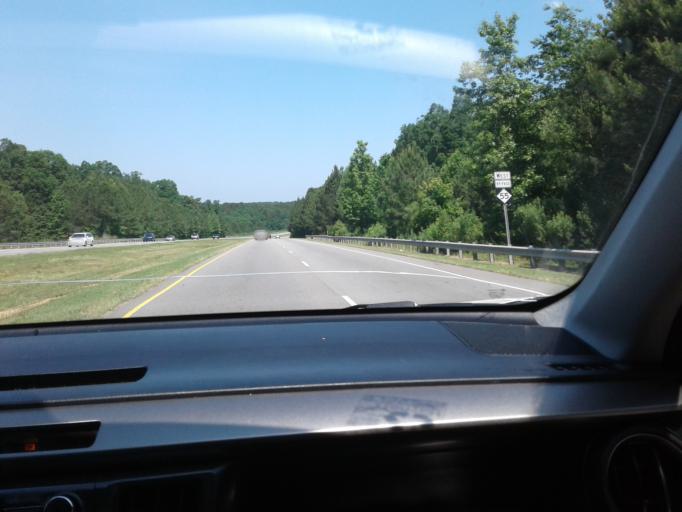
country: US
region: North Carolina
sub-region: Wake County
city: Holly Springs
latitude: 35.6444
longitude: -78.8411
